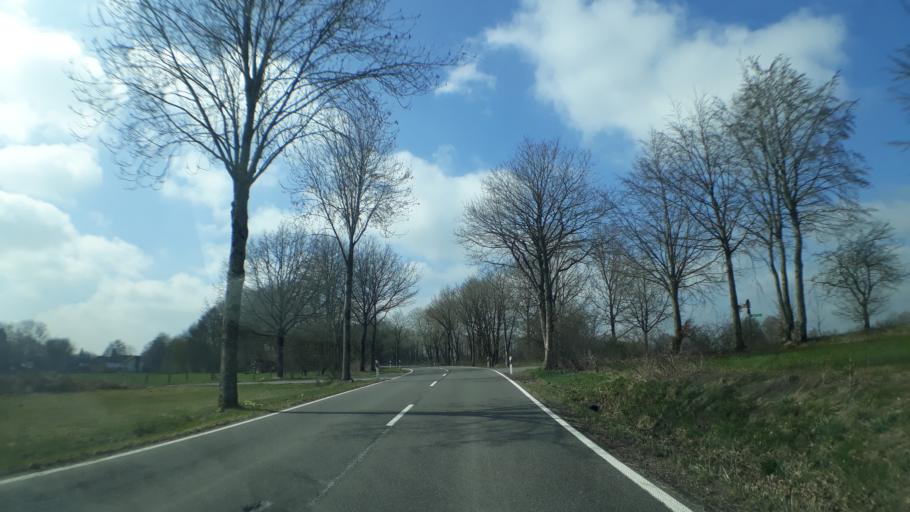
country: DE
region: North Rhine-Westphalia
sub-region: Regierungsbezirk Koln
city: Monschau
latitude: 50.5442
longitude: 6.2583
